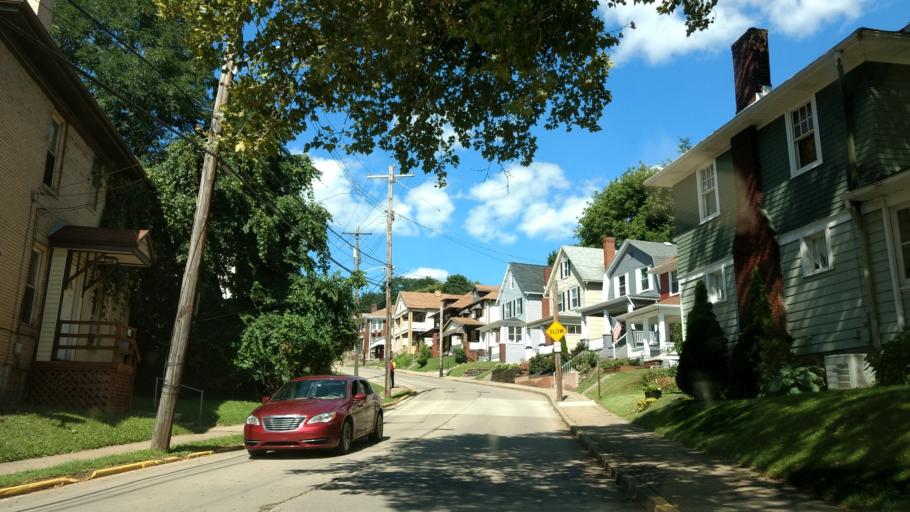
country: US
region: Pennsylvania
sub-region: Allegheny County
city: Avalon
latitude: 40.4970
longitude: -80.0659
